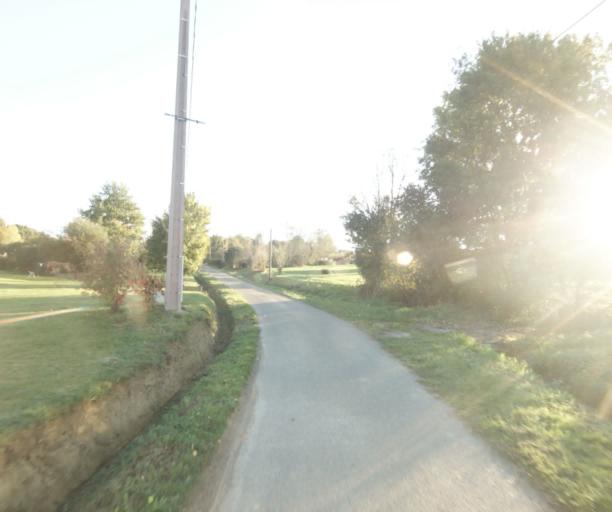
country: FR
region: Midi-Pyrenees
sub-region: Departement du Gers
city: Eauze
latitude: 43.7436
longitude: 0.1663
